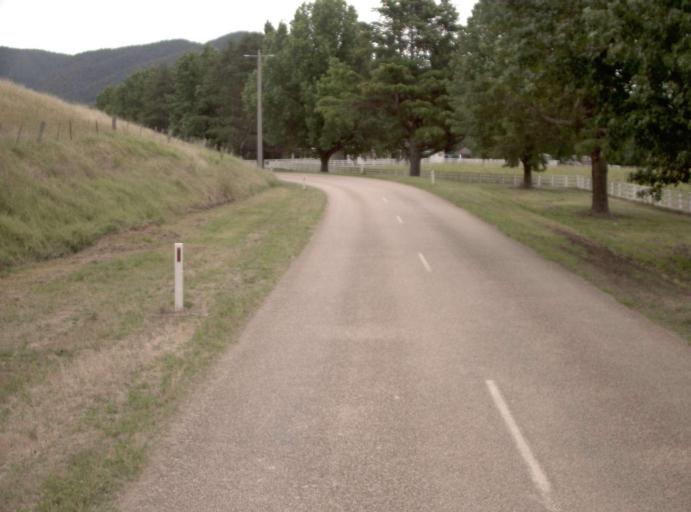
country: AU
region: Victoria
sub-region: East Gippsland
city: Bairnsdale
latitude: -37.4680
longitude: 147.2540
